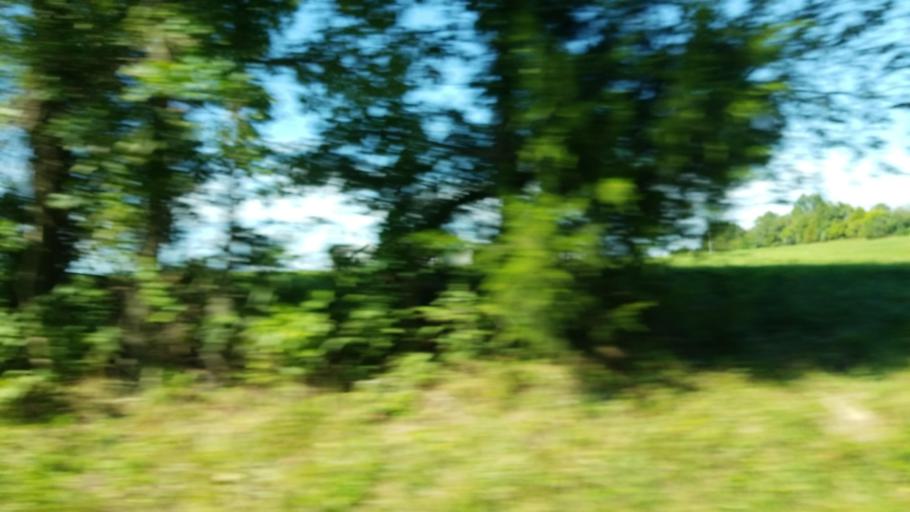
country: US
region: Illinois
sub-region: Williamson County
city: Johnston City
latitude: 37.7868
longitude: -88.7856
